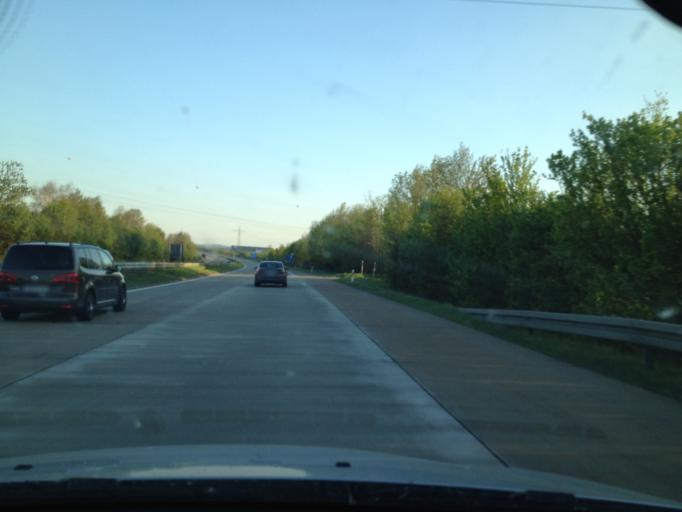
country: DE
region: Bavaria
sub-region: Regierungsbezirk Mittelfranken
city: Neusitz
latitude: 49.3746
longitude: 10.2140
